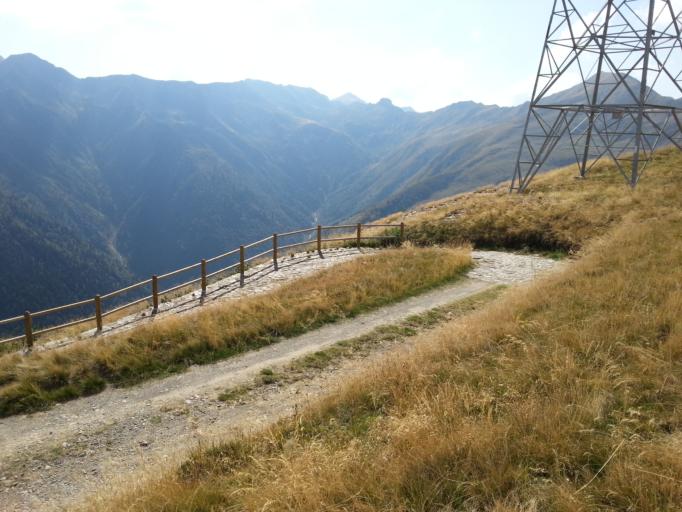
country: IT
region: Lombardy
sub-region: Provincia di Como
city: San Bartolomeo Val Cavargna
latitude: 46.1558
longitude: 9.1699
